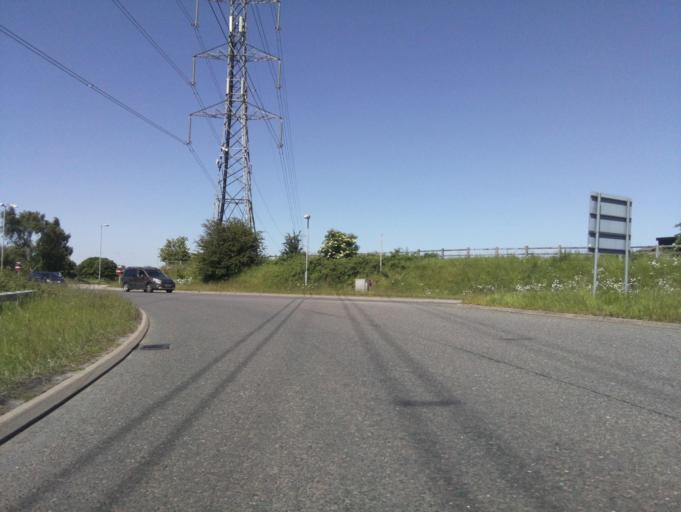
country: GB
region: England
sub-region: Cumbria
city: Scotby
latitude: 54.8955
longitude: -2.8856
